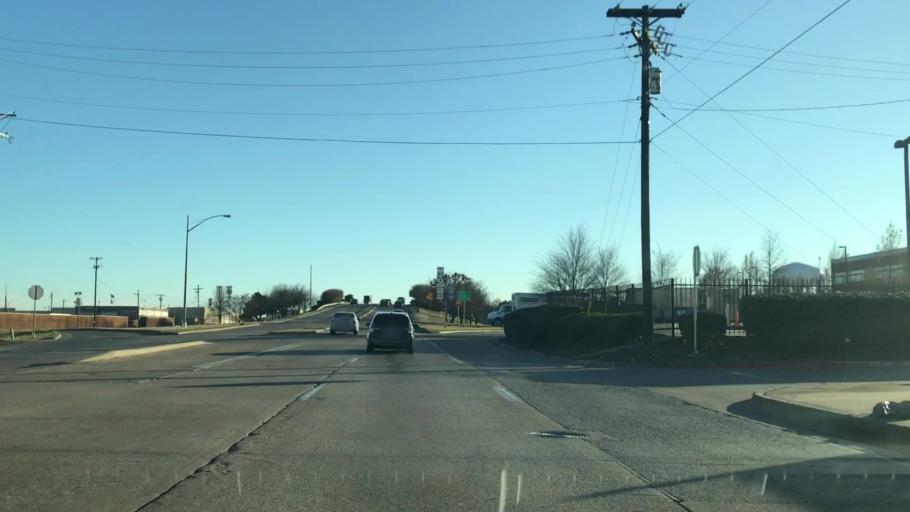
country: US
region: Texas
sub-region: Dallas County
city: Mesquite
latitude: 32.7998
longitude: -96.6683
